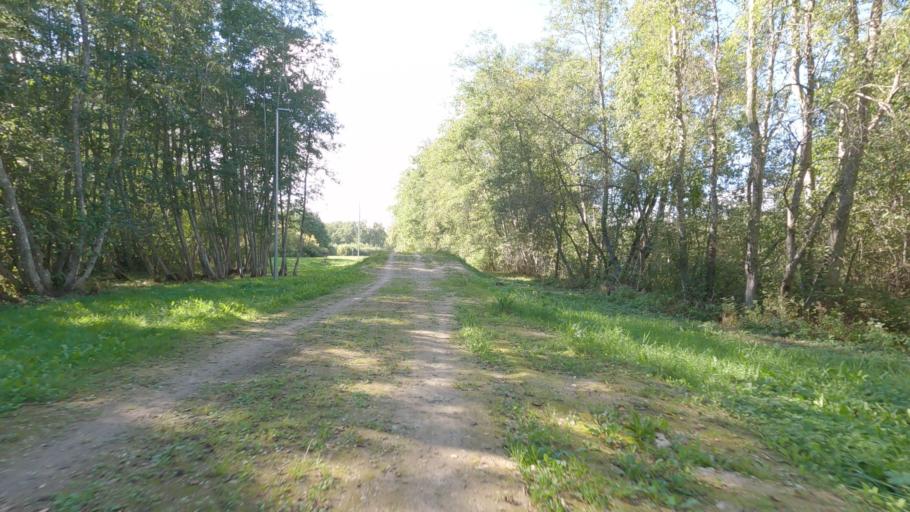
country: EE
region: Raplamaa
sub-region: Rapla vald
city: Rapla
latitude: 58.9986
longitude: 24.8240
